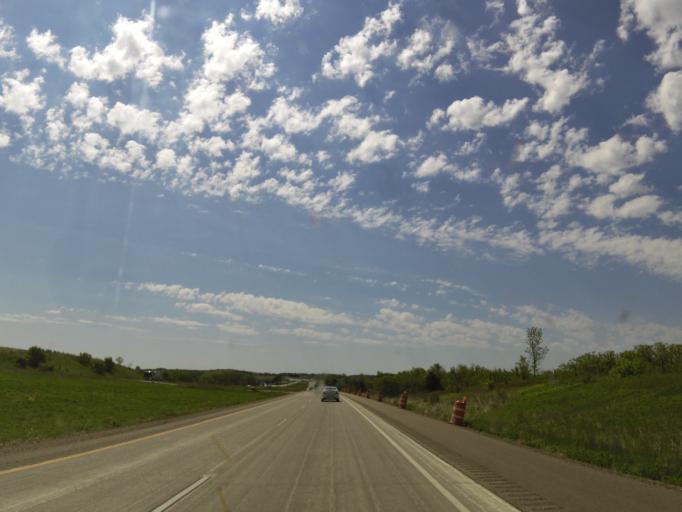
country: US
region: Wisconsin
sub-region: Trempealeau County
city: Osseo
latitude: 44.6504
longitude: -91.3104
